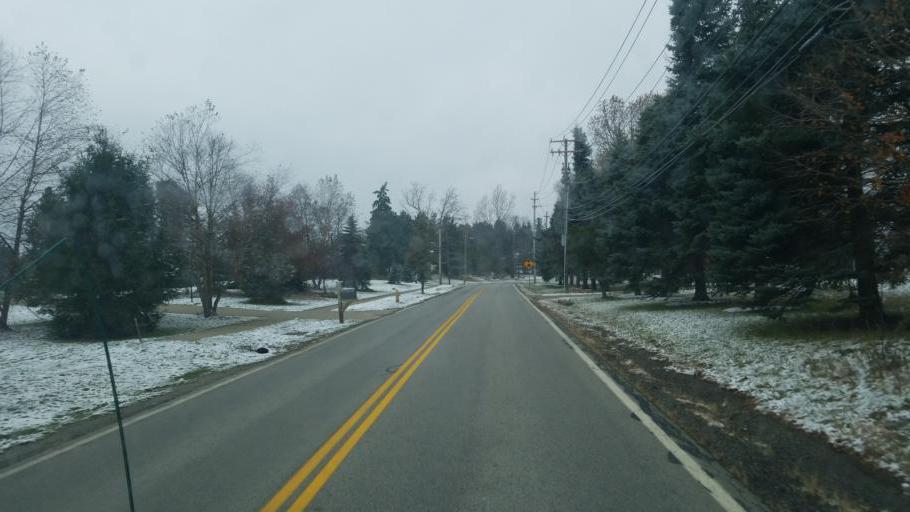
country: US
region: Ohio
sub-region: Cuyahoga County
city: Broadview Heights
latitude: 41.2885
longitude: -81.6549
